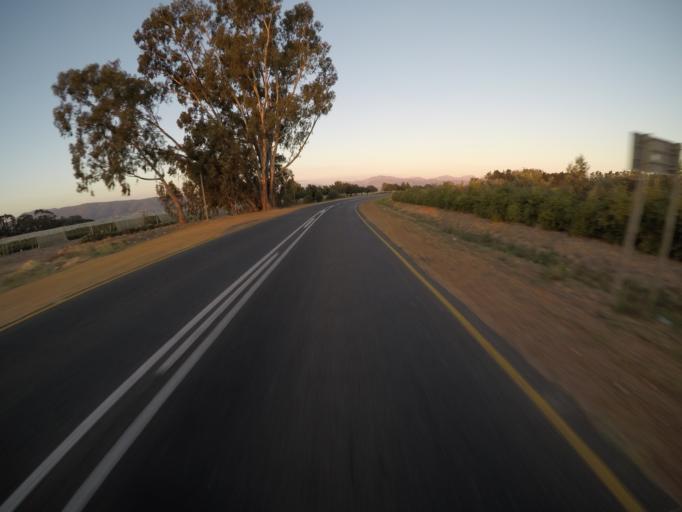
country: ZA
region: Western Cape
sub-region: Cape Winelands District Municipality
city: Paarl
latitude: -33.8034
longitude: 18.8883
